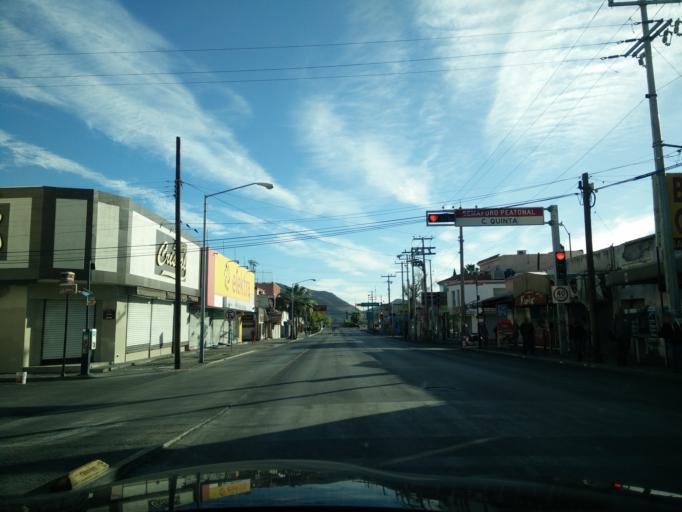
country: MX
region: Chihuahua
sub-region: Chihuahua
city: Chihuahua
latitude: 28.6399
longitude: -106.0770
